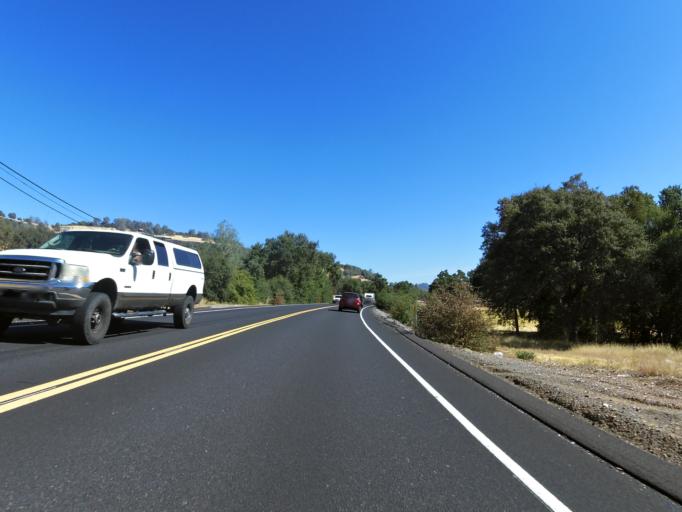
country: US
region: California
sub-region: Calaveras County
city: Murphys
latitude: 38.1012
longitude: -120.4695
